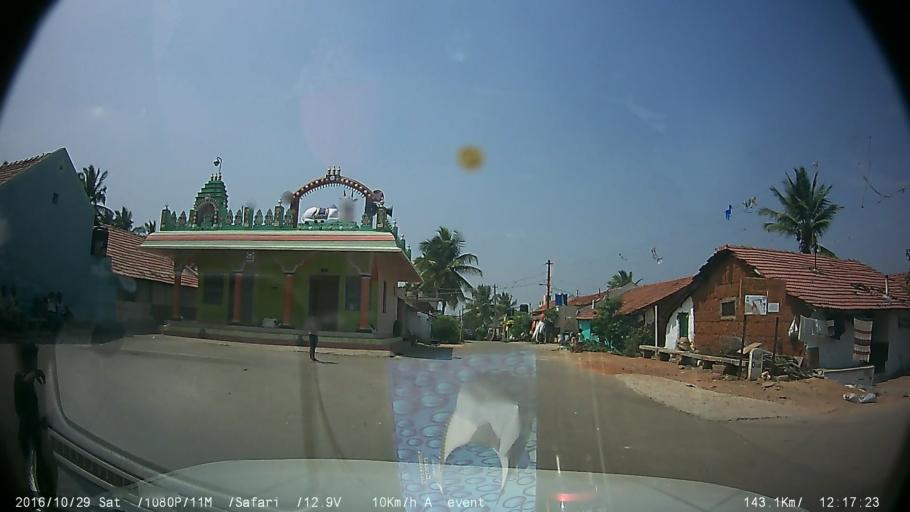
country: IN
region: Karnataka
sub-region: Mysore
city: Mysore
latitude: 12.3782
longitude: 76.5823
